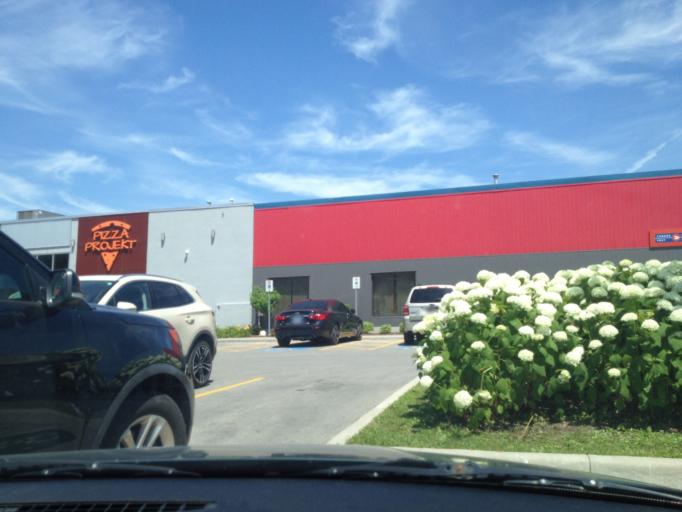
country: CA
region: Ontario
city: London
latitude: 42.9869
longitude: -81.2866
